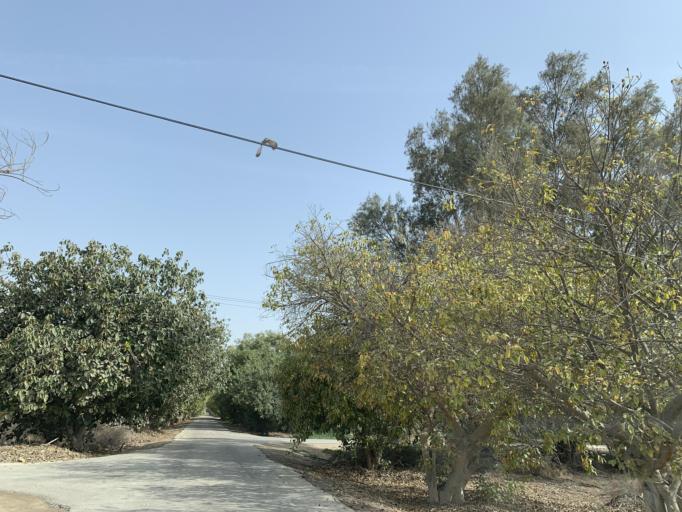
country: BH
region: Northern
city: Madinat `Isa
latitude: 26.1647
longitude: 50.5304
